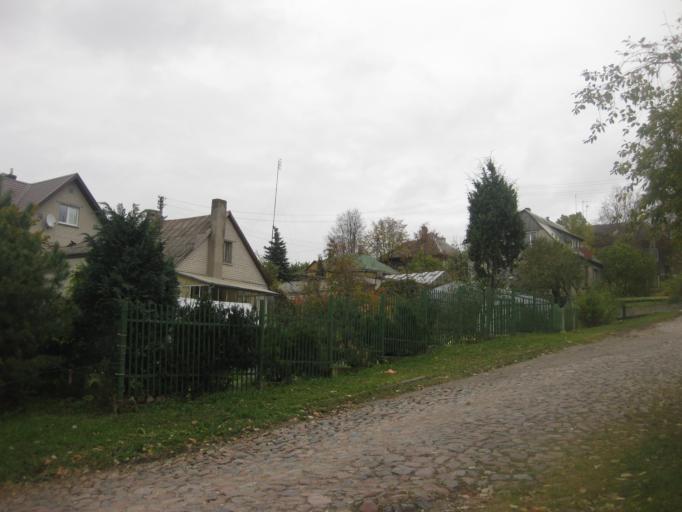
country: LT
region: Kauno apskritis
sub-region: Kaunas
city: Kaunas
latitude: 54.9090
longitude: 23.9099
